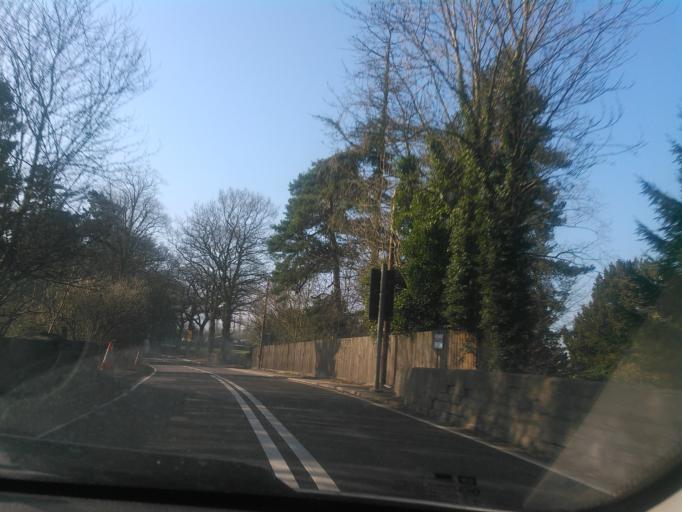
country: GB
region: England
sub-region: Shropshire
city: Craven Arms
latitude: 52.4571
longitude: -2.8368
